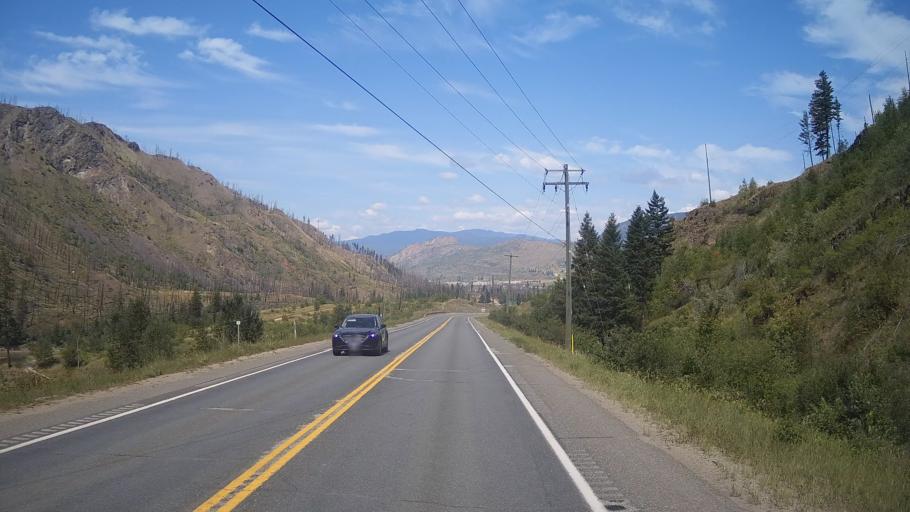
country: CA
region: British Columbia
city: Kamloops
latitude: 51.1092
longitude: -120.1372
